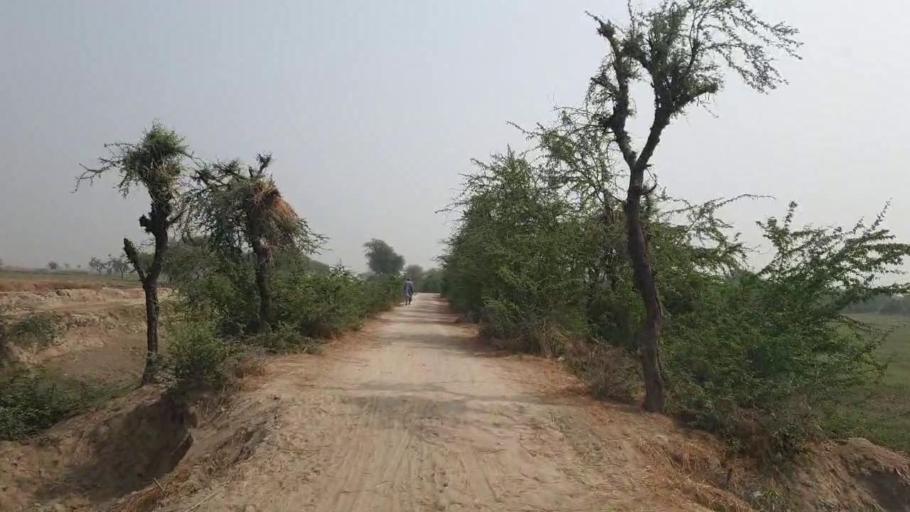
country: PK
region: Sindh
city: Kario
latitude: 24.6505
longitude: 68.6088
